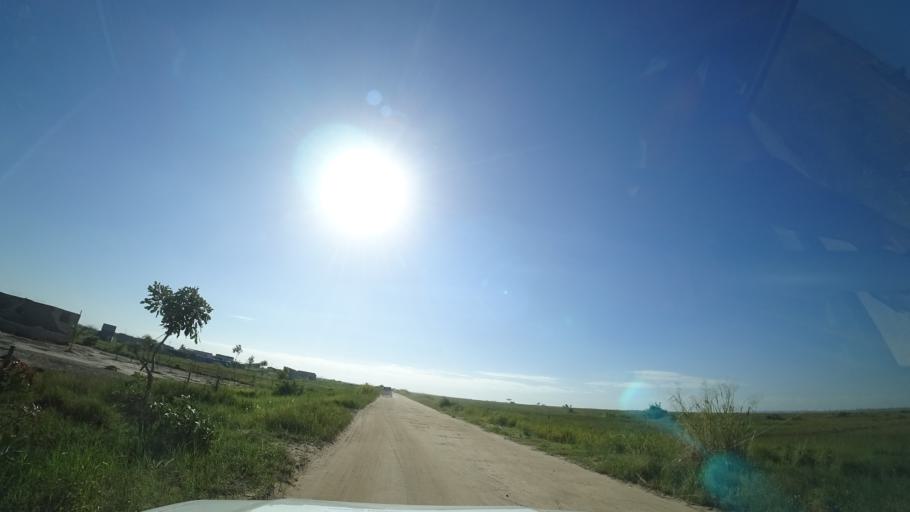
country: MZ
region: Sofala
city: Beira
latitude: -19.7616
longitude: 34.9097
